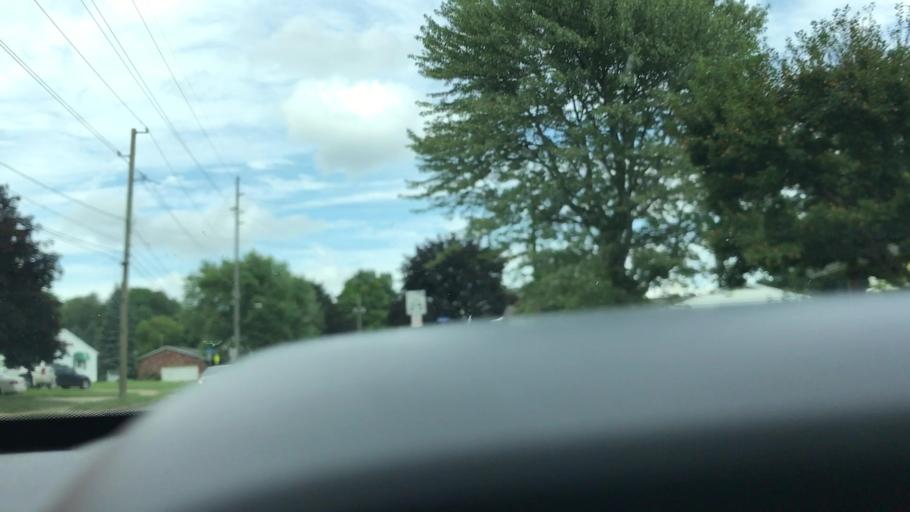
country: US
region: Ohio
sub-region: Stark County
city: Massillon
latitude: 40.8127
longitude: -81.5222
